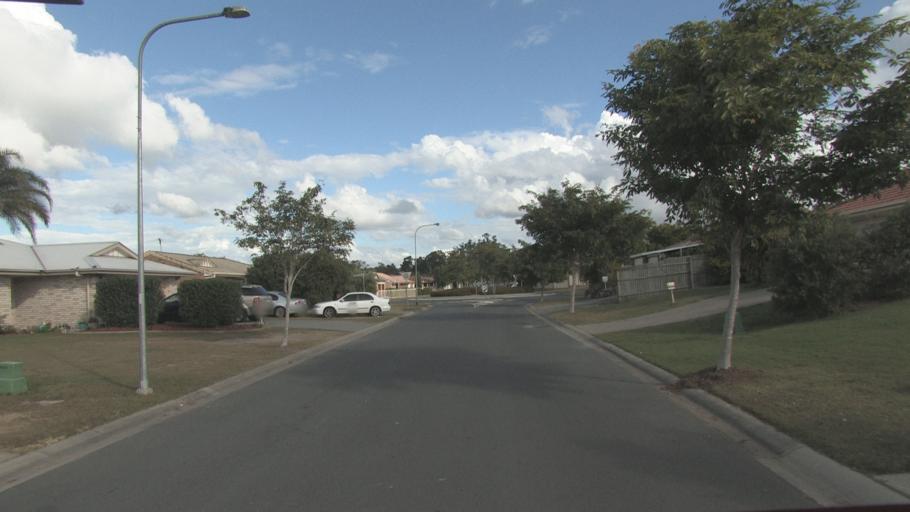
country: AU
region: Queensland
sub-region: Logan
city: Logan Reserve
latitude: -27.6951
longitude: 153.0851
